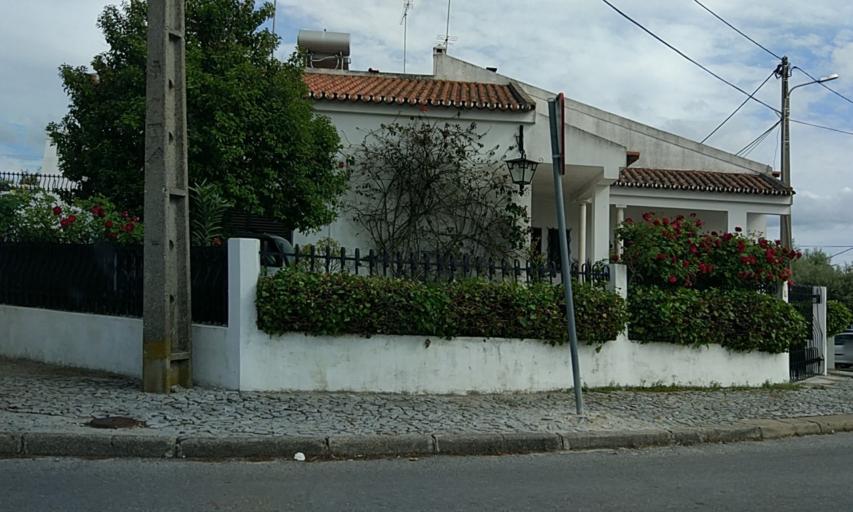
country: PT
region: Evora
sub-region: Evora
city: Evora
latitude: 38.5674
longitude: -7.9305
